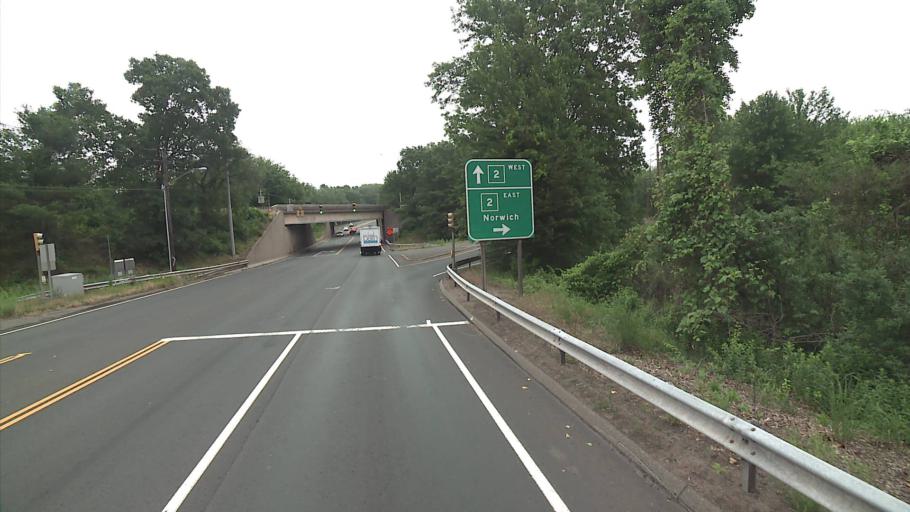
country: US
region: Connecticut
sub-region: Hartford County
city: Glastonbury
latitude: 41.7141
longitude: -72.5964
